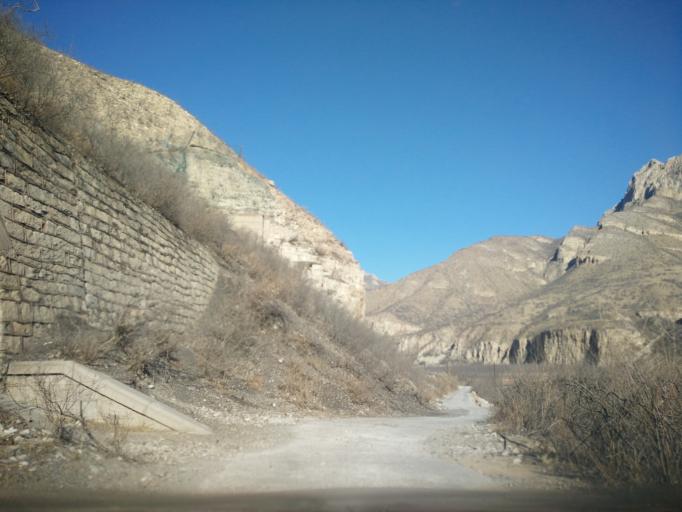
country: CN
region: Beijing
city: Zhaitang
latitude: 40.1619
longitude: 115.6685
